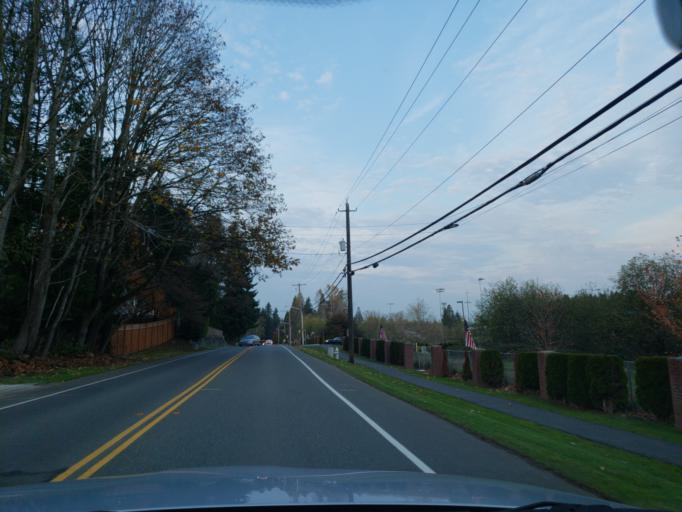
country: US
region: Washington
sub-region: King County
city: Kingsgate
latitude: 47.7435
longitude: -122.1916
